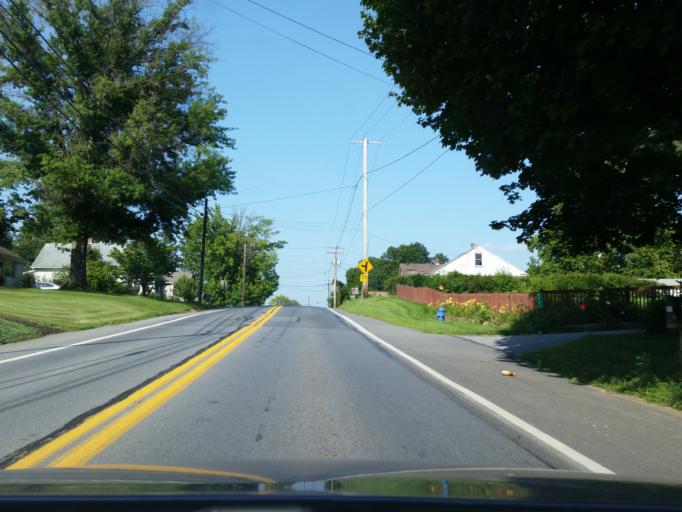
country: US
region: Pennsylvania
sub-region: Lancaster County
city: Mount Joy
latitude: 40.1169
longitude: -76.4977
